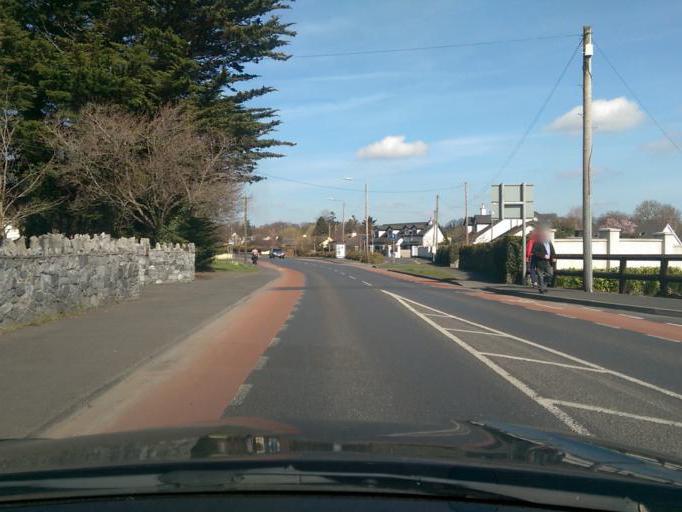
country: IE
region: Leinster
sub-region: Kildare
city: Celbridge
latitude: 53.3453
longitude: -6.5423
